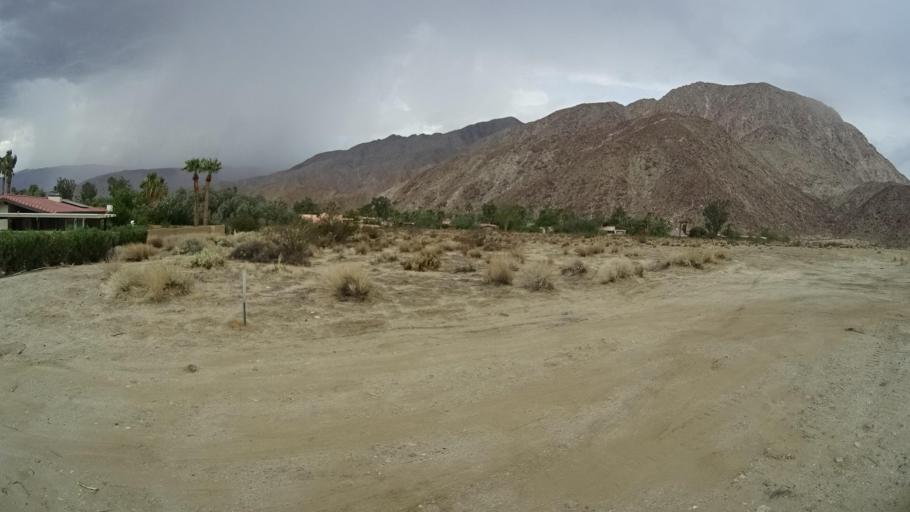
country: US
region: California
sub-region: San Diego County
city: Borrego Springs
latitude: 33.2884
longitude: -116.3953
